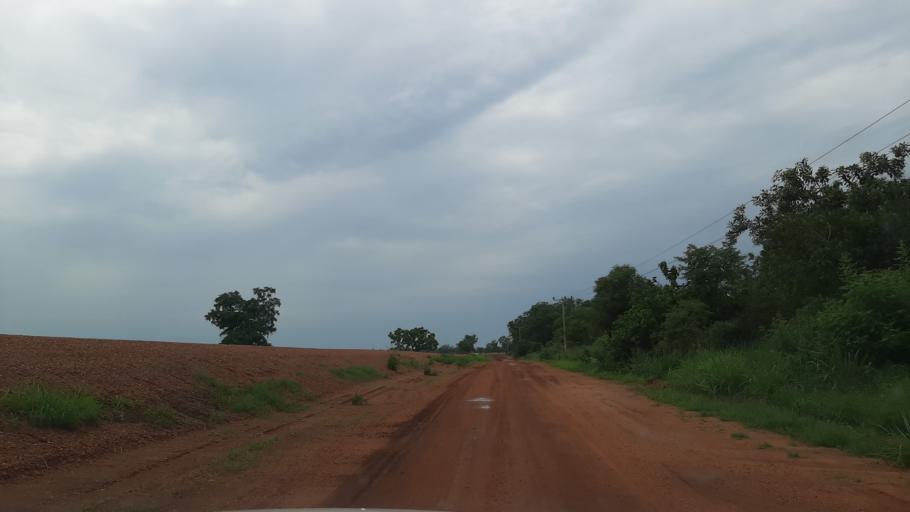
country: ET
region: Gambela
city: Gambela
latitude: 8.1476
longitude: 34.3583
